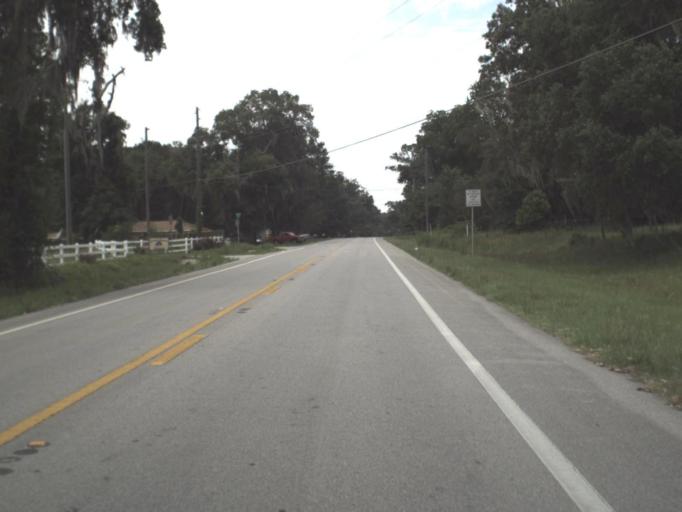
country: US
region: Florida
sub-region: Madison County
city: Madison
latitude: 30.4863
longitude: -83.4180
